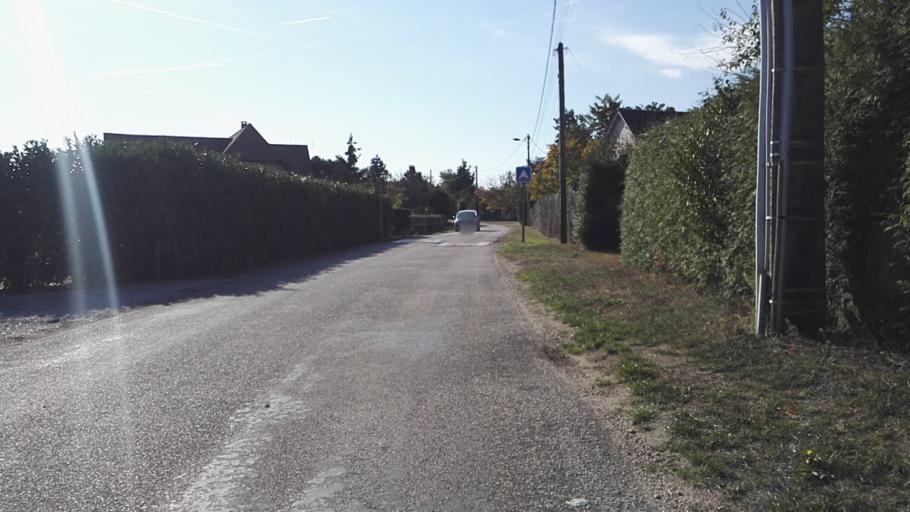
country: FR
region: Haute-Normandie
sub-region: Departement de l'Eure
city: Menilles
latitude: 49.0441
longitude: 1.3382
